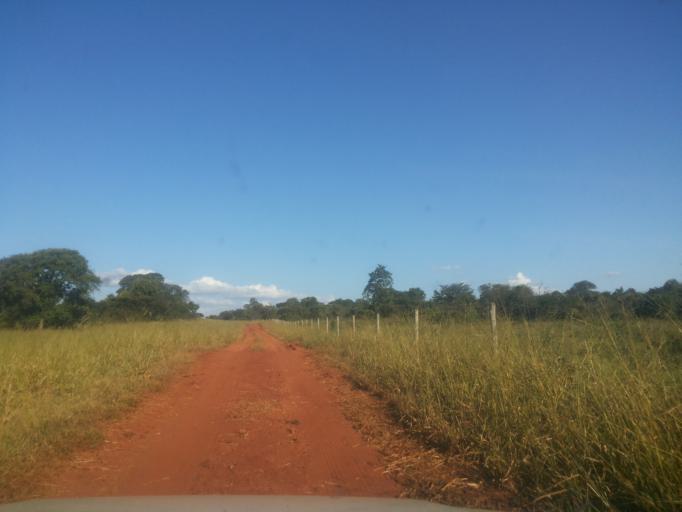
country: BR
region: Minas Gerais
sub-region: Santa Vitoria
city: Santa Vitoria
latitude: -19.0111
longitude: -50.4524
